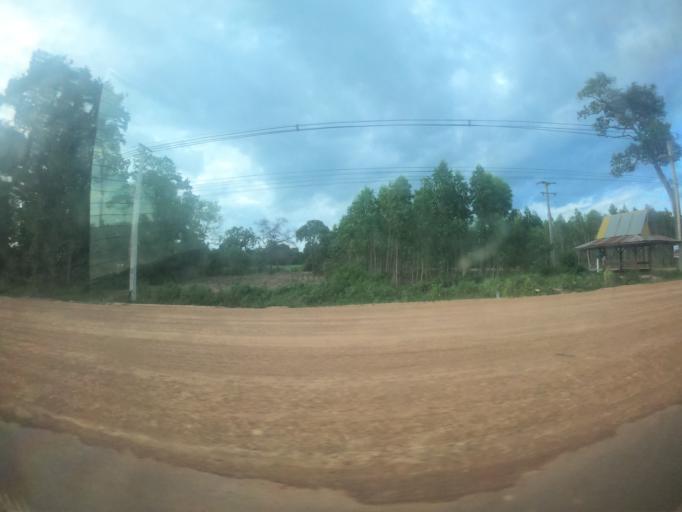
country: TH
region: Surin
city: Kap Choeng
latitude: 14.4621
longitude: 103.6530
